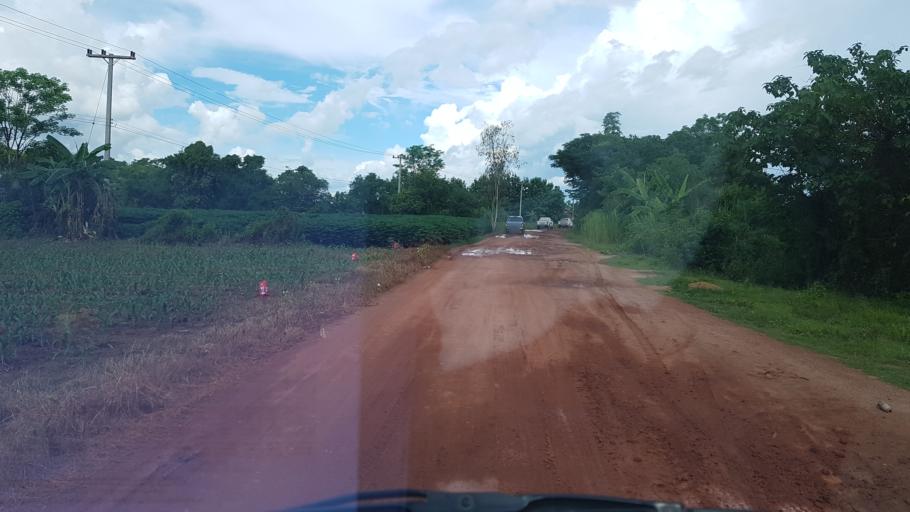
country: LA
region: Vientiane
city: Vientiane
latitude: 18.2372
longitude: 102.5587
